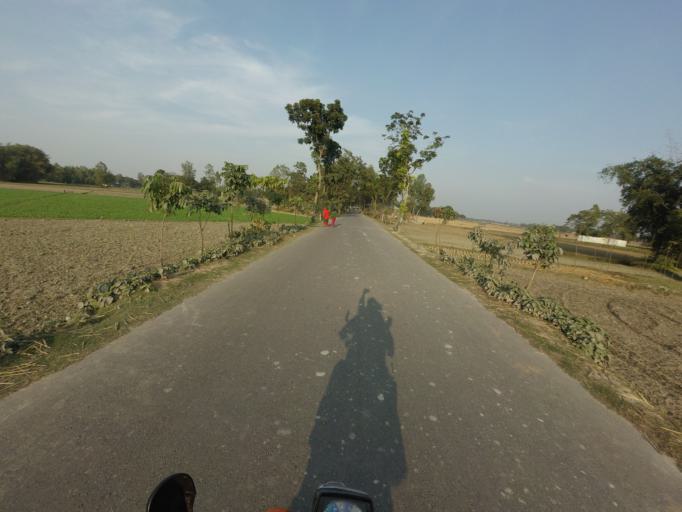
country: BD
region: Rajshahi
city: Saidpur
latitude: 25.9988
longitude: 88.7507
